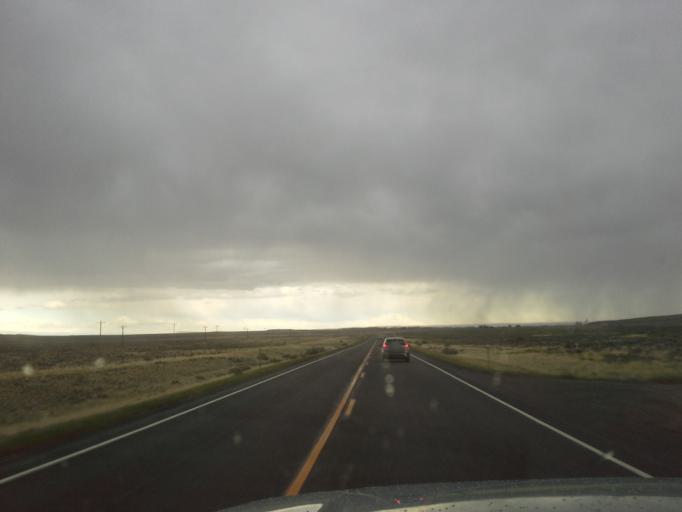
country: US
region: Wyoming
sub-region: Park County
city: Powell
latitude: 45.0334
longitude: -108.6406
